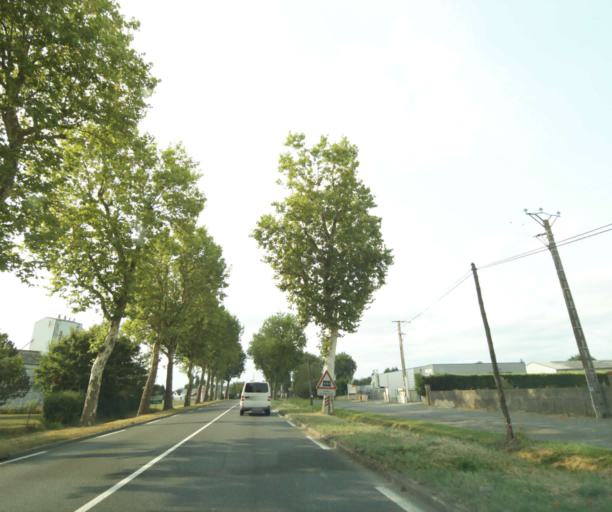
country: FR
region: Centre
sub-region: Departement d'Indre-et-Loire
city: Cormery
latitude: 47.2612
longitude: 0.8375
